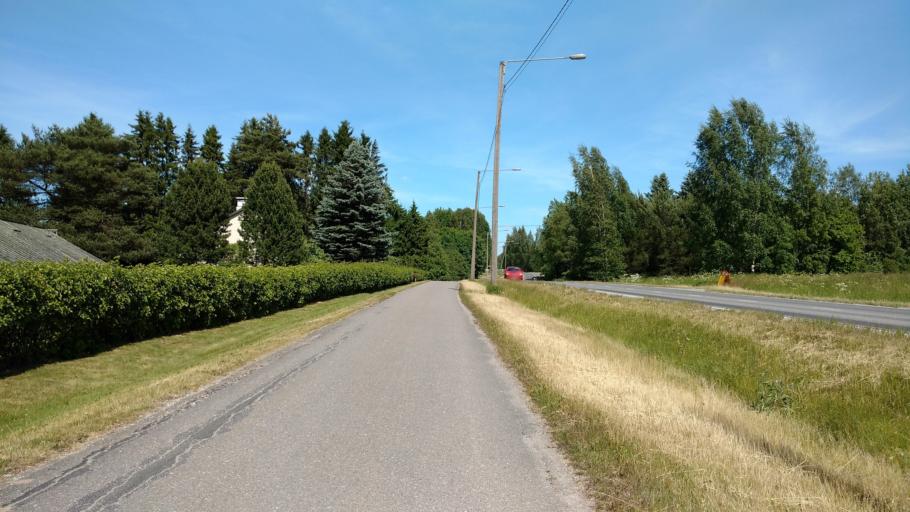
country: FI
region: Varsinais-Suomi
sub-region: Salo
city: Salo
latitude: 60.4008
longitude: 23.1611
